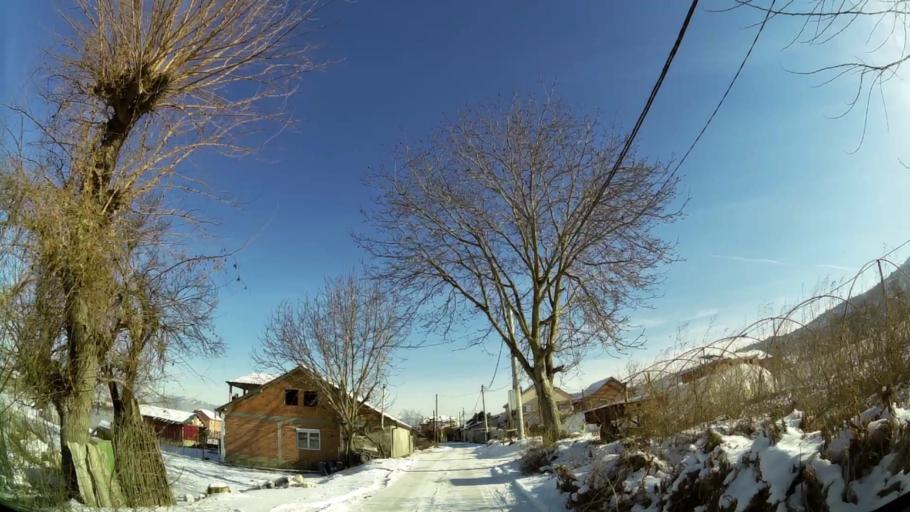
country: MK
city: Grchec
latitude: 41.9861
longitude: 21.3283
